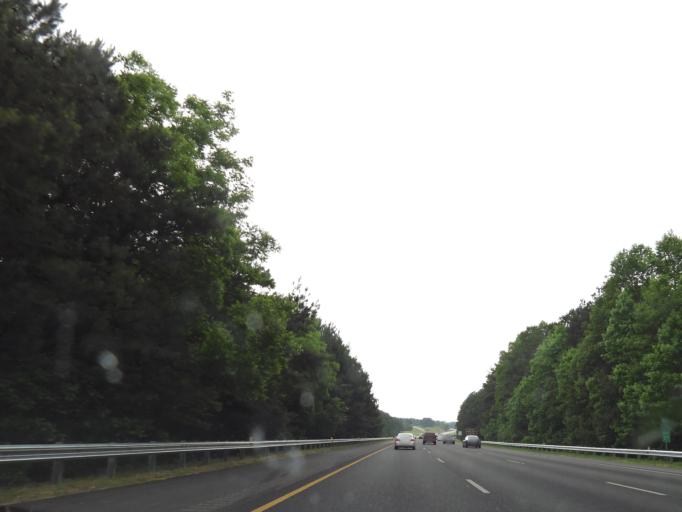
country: US
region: Georgia
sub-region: Carroll County
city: Villa Rica
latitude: 33.7231
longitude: -84.8885
